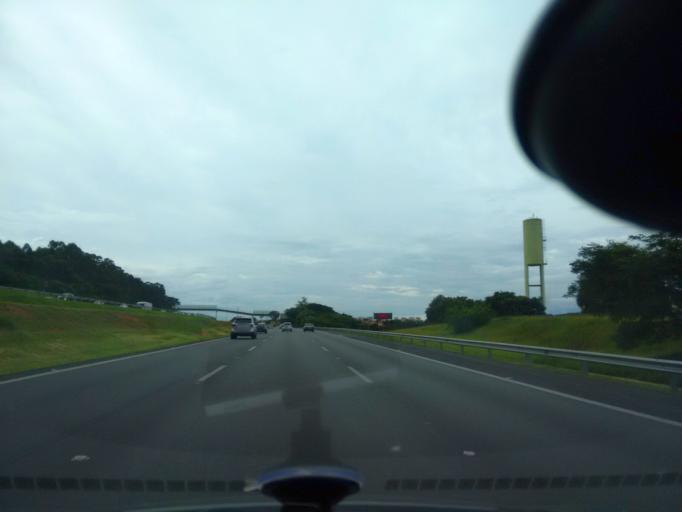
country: BR
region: Sao Paulo
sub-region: Campinas
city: Campinas
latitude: -22.9439
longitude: -47.1257
